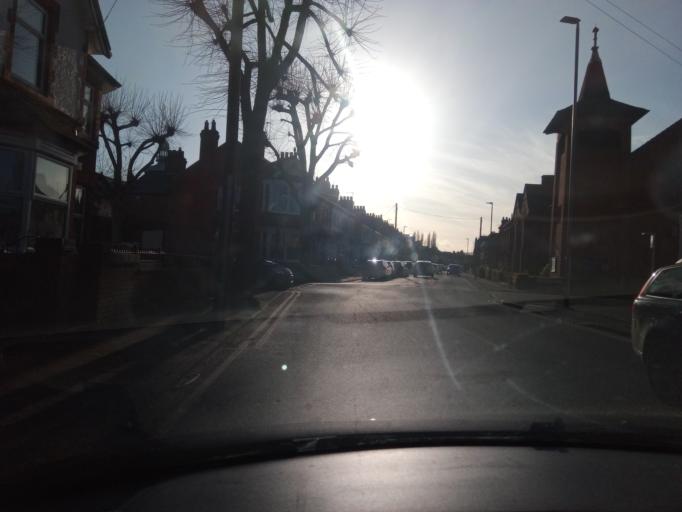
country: GB
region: England
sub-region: Leicestershire
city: Loughborough
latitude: 52.7713
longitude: -1.2108
